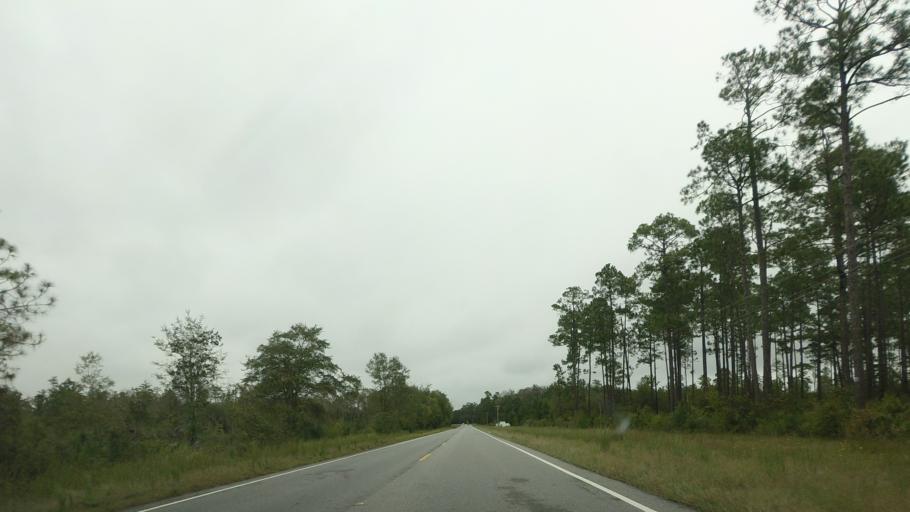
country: US
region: Georgia
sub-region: Berrien County
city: Nashville
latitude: 31.2970
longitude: -83.2350
